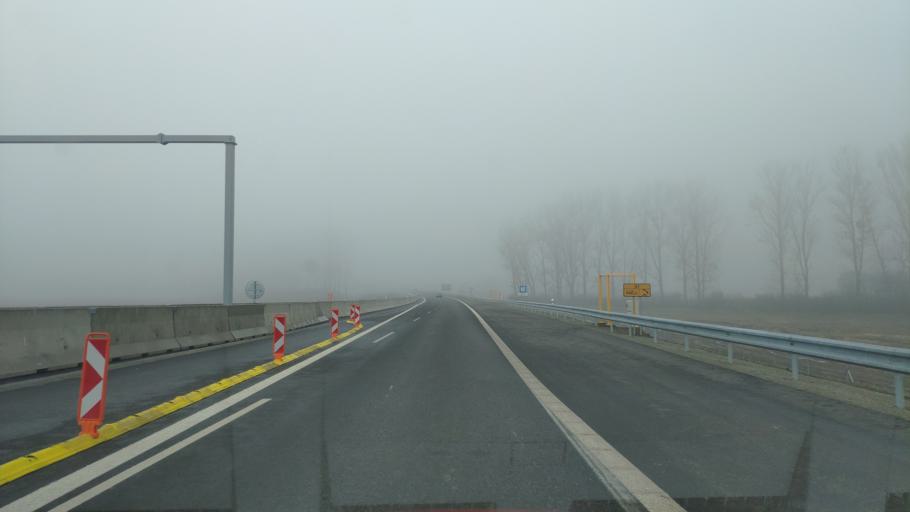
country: SK
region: Kosicky
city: Kosice
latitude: 48.7253
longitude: 21.4325
